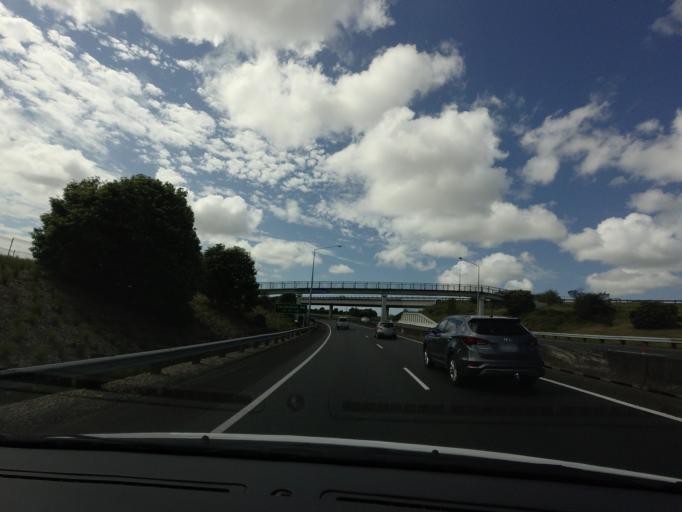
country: NZ
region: Auckland
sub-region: Auckland
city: Mangere
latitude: -36.9637
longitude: 174.7995
